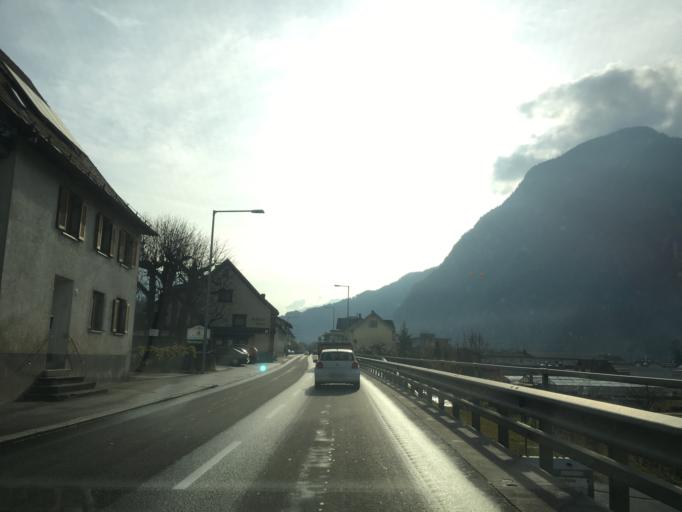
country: AT
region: Vorarlberg
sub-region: Politischer Bezirk Bludenz
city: Bludenz
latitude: 47.1495
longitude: 9.8263
